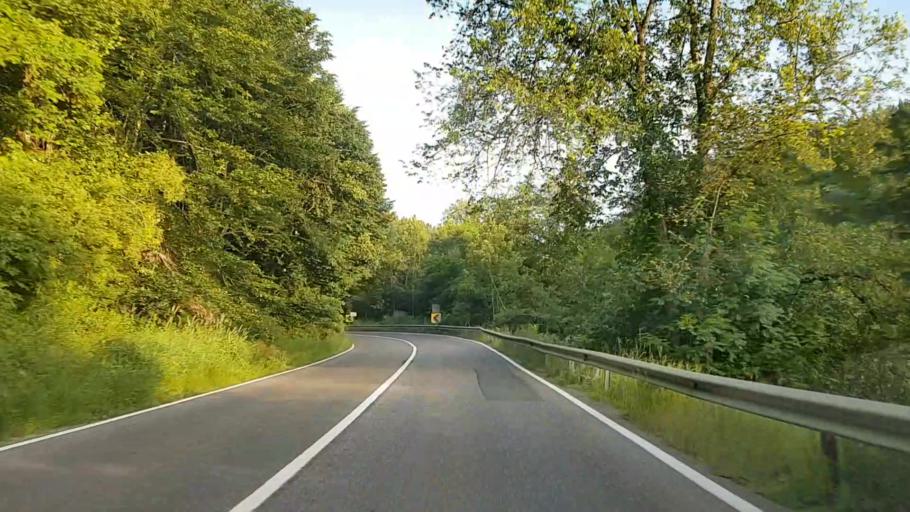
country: RO
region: Harghita
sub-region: Comuna Corund
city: Corund
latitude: 46.4520
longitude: 25.2130
